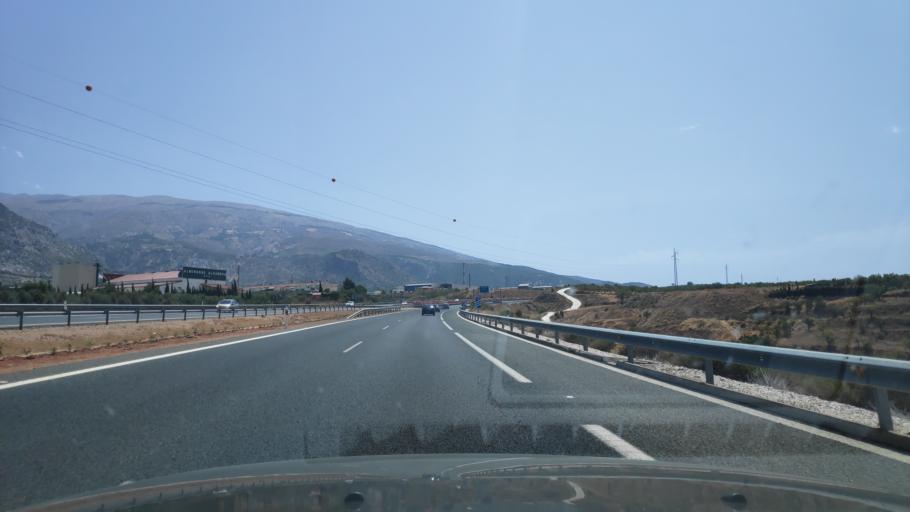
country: ES
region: Andalusia
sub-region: Provincia de Granada
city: Durcal
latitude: 36.9796
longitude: -3.5686
